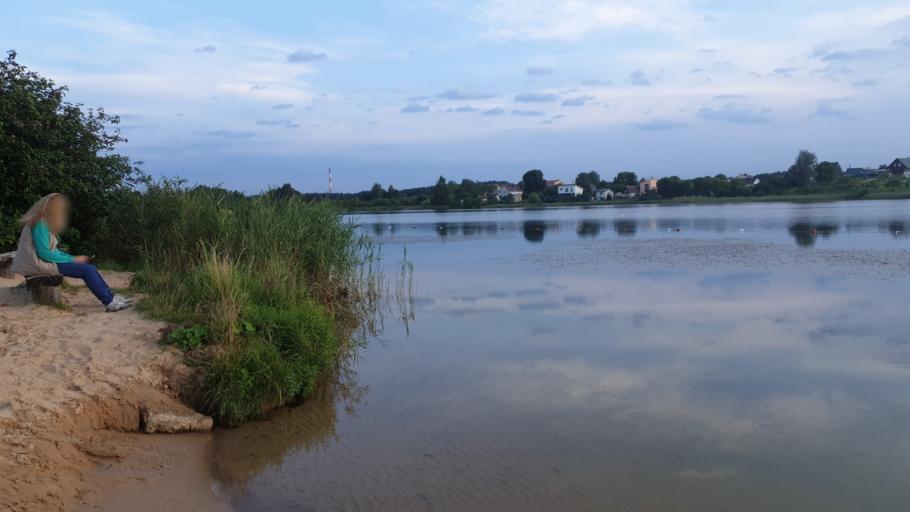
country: LT
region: Vilnius County
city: Pilaite
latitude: 54.7056
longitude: 25.1594
